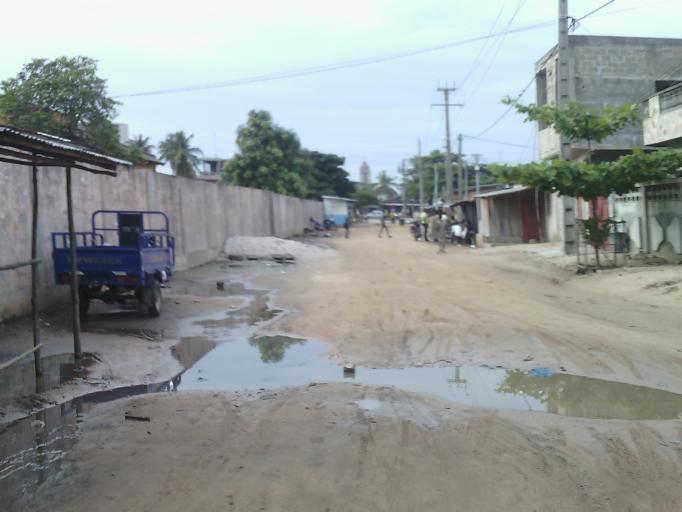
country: BJ
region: Atlantique
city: Abomey-Calavi
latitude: 6.3913
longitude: 2.3618
